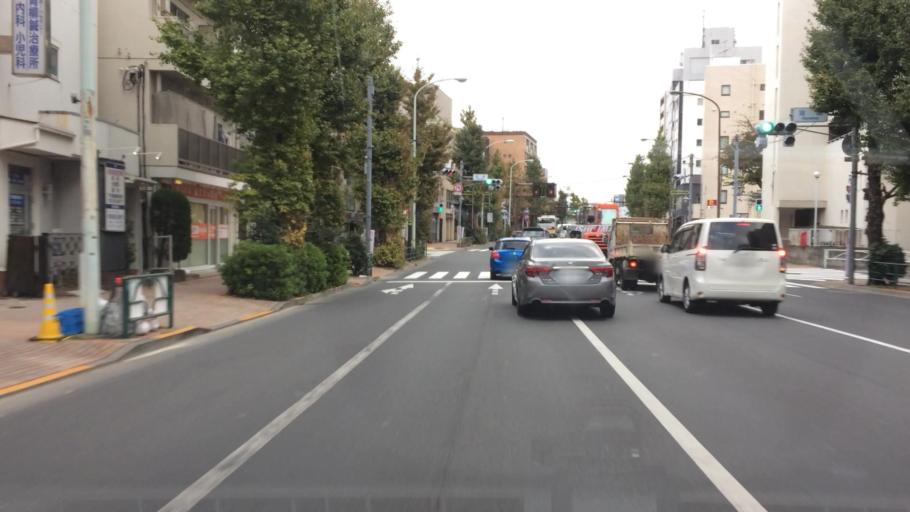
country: JP
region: Tokyo
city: Tokyo
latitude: 35.6303
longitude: 139.7007
